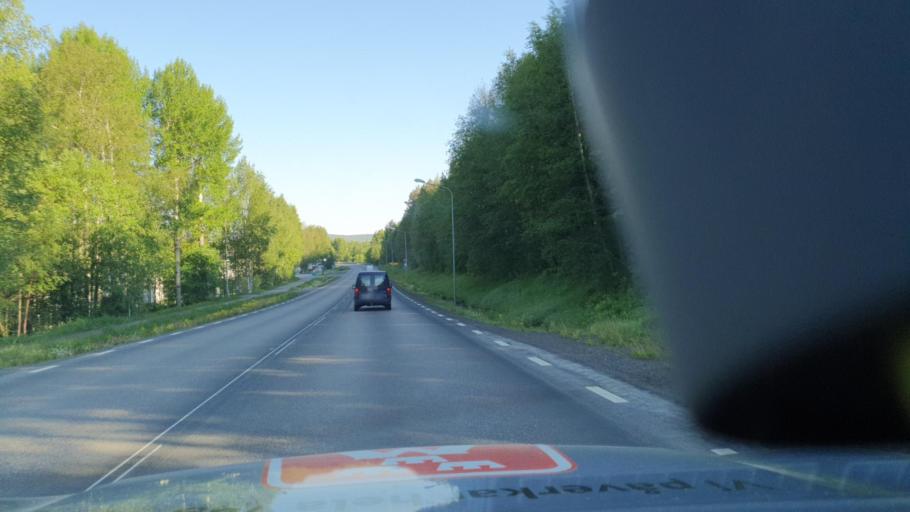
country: SE
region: Norrbotten
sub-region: Bodens Kommun
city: Boden
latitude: 65.8422
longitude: 21.6045
